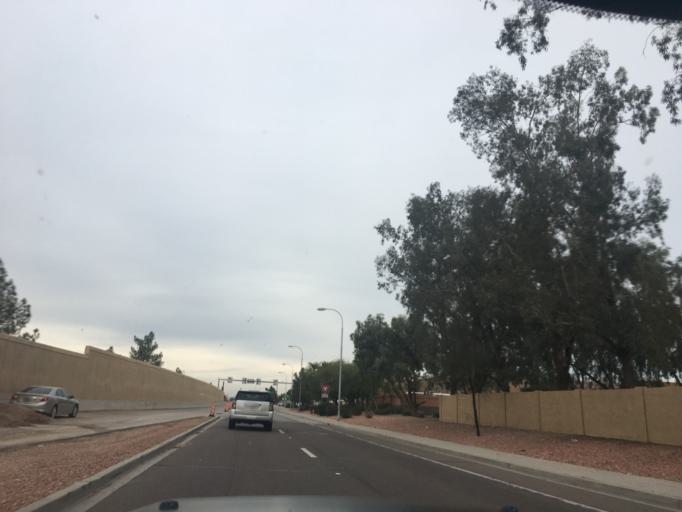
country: US
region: Arizona
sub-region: Maricopa County
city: San Carlos
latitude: 33.3328
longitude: -111.8924
